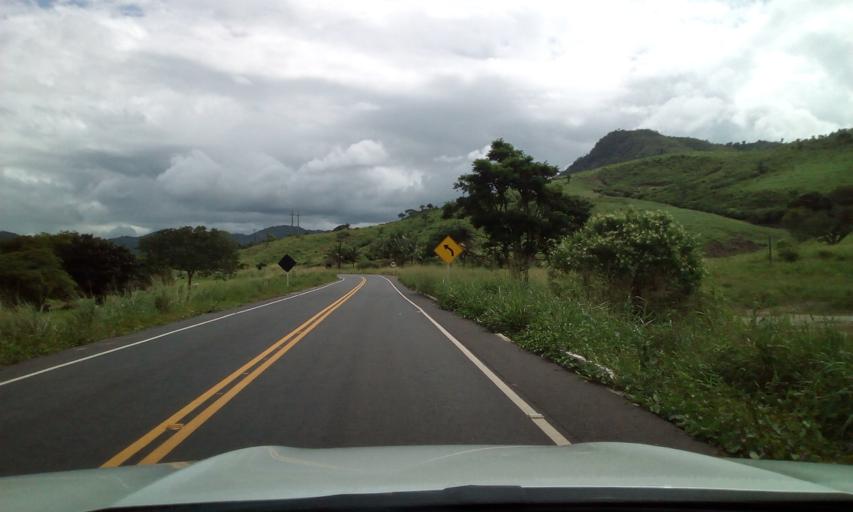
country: BR
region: Paraiba
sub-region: Alagoinha
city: Alagoinha
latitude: -6.8953
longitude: -35.5411
